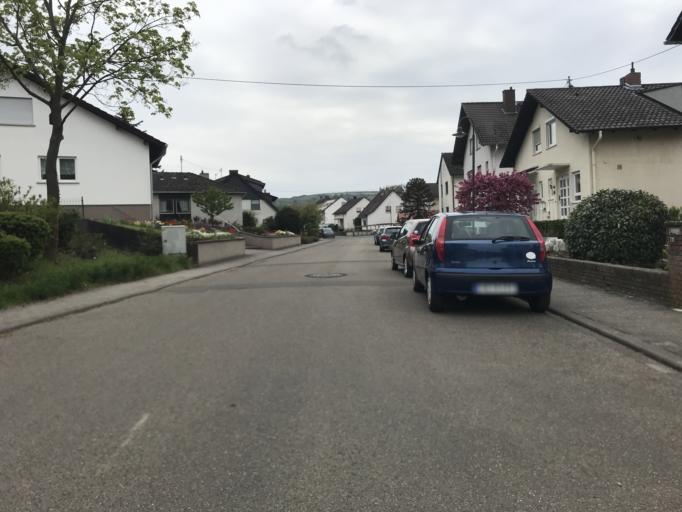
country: DE
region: Rheinland-Pfalz
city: Gau-Algesheim
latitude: 49.9525
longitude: 8.0183
